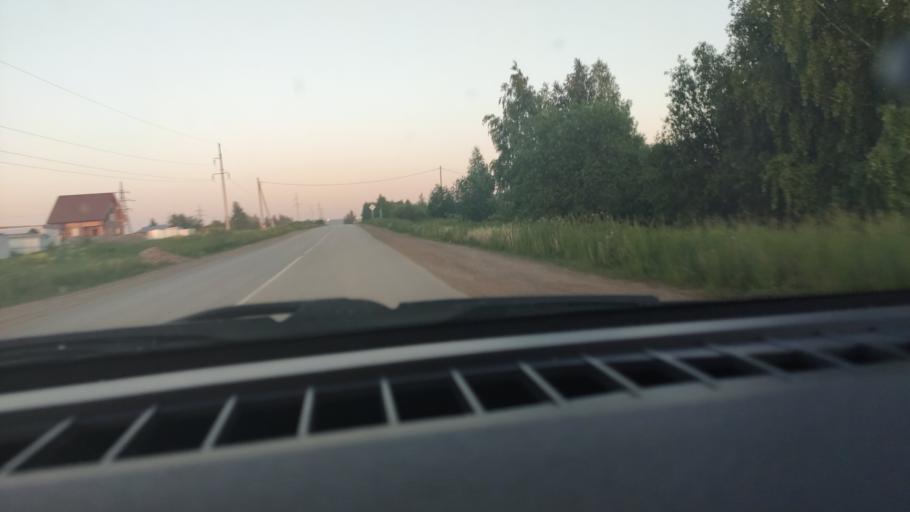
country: RU
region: Perm
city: Kultayevo
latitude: 57.8917
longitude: 55.9170
